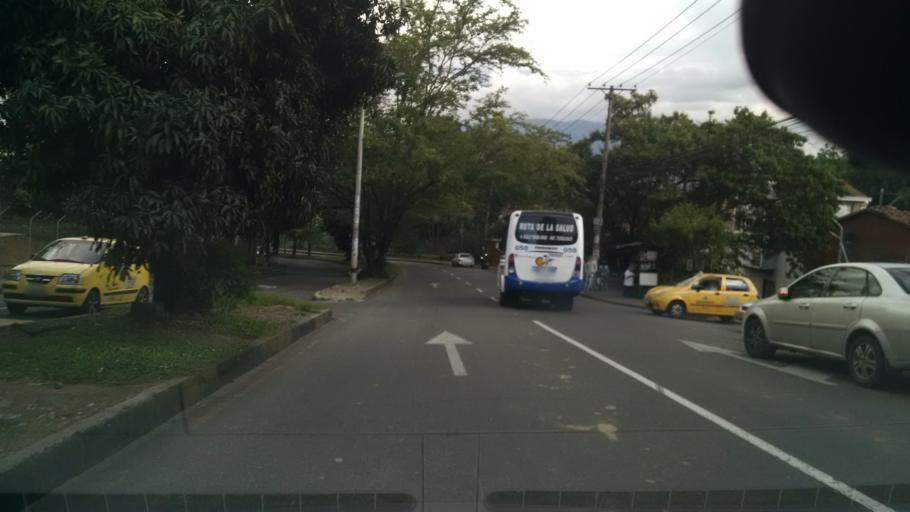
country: CO
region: Antioquia
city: Medellin
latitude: 6.2766
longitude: -75.5807
